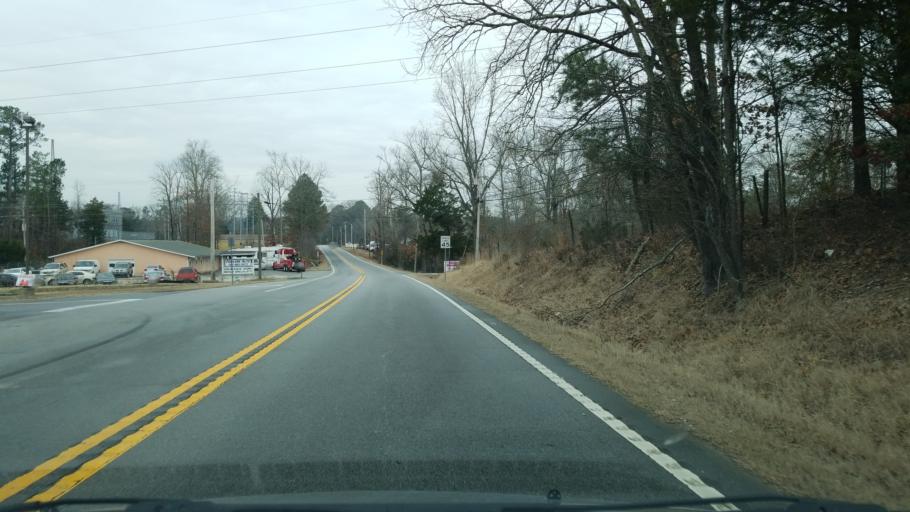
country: US
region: Georgia
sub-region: Catoosa County
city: Indian Springs
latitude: 34.9608
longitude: -85.1677
